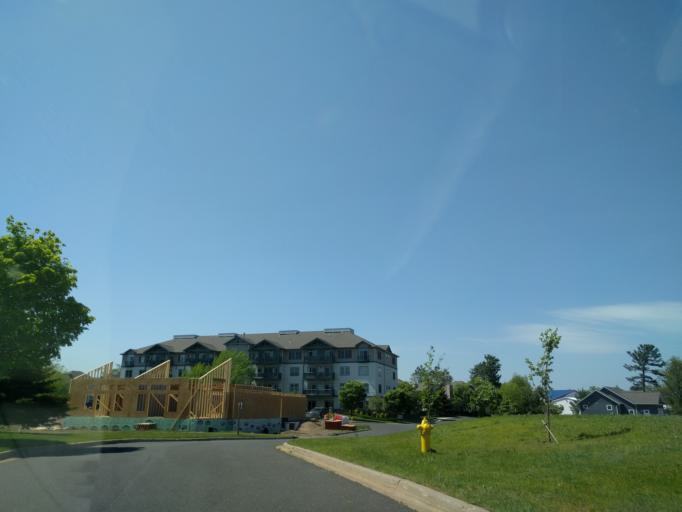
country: US
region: Michigan
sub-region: Marquette County
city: Marquette
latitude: 46.5549
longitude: -87.3843
